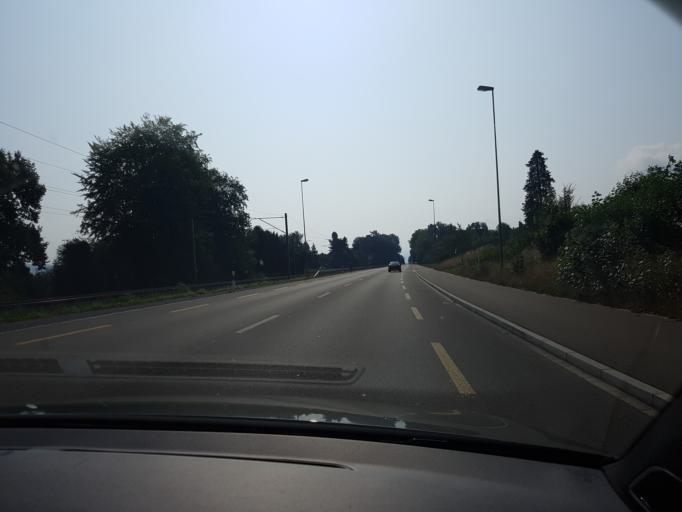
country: CH
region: Zurich
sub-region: Bezirk Horgen
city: Au / Mittel-Dorf
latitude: 47.2453
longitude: 8.6516
